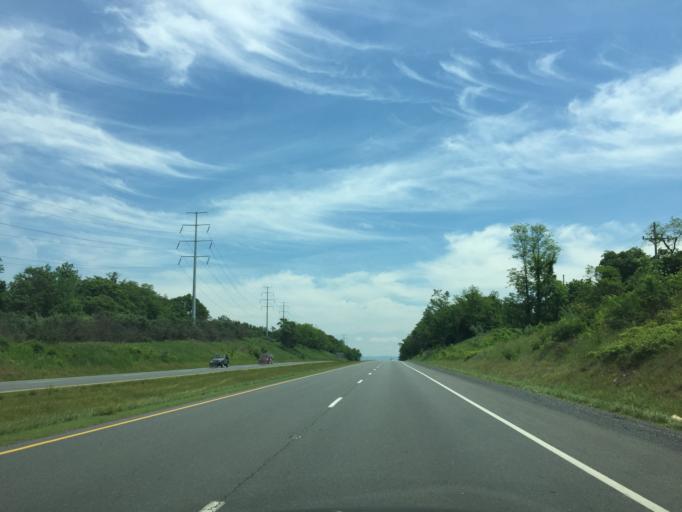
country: US
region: Virginia
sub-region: City of Winchester
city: Winchester
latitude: 39.2129
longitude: -78.1684
